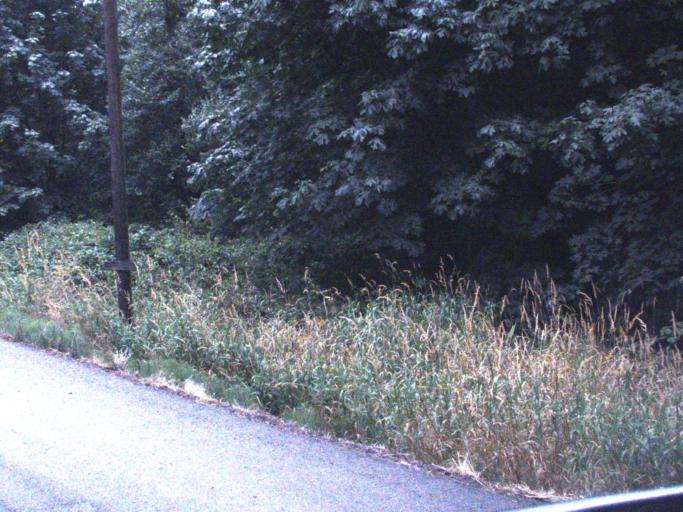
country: US
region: Washington
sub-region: King County
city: Duvall
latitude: 47.7908
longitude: -121.9746
